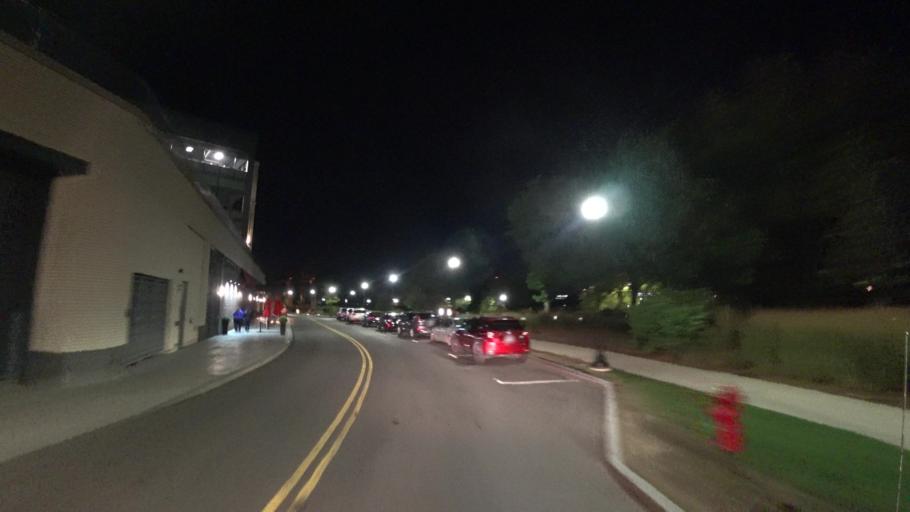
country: US
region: Massachusetts
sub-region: Middlesex County
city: Somerville
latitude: 42.3955
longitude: -71.0784
